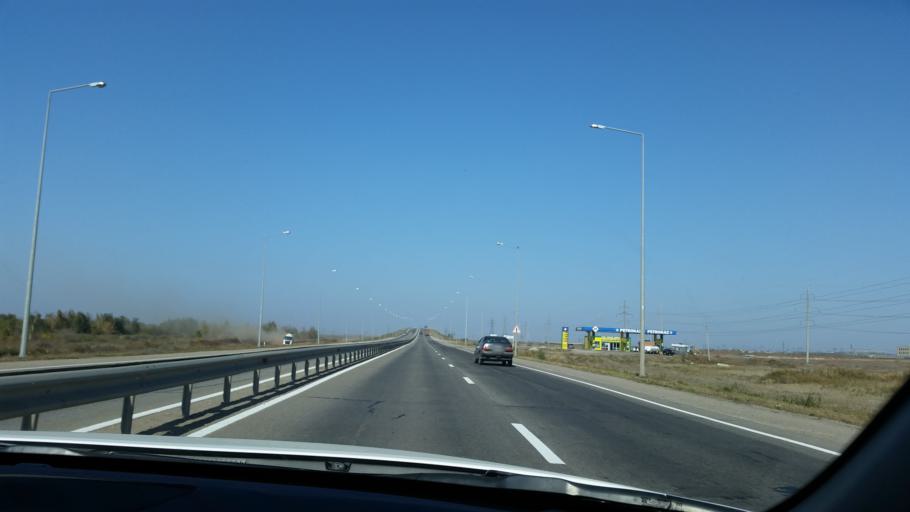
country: KZ
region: Astana Qalasy
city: Astana
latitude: 51.2187
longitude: 71.3203
